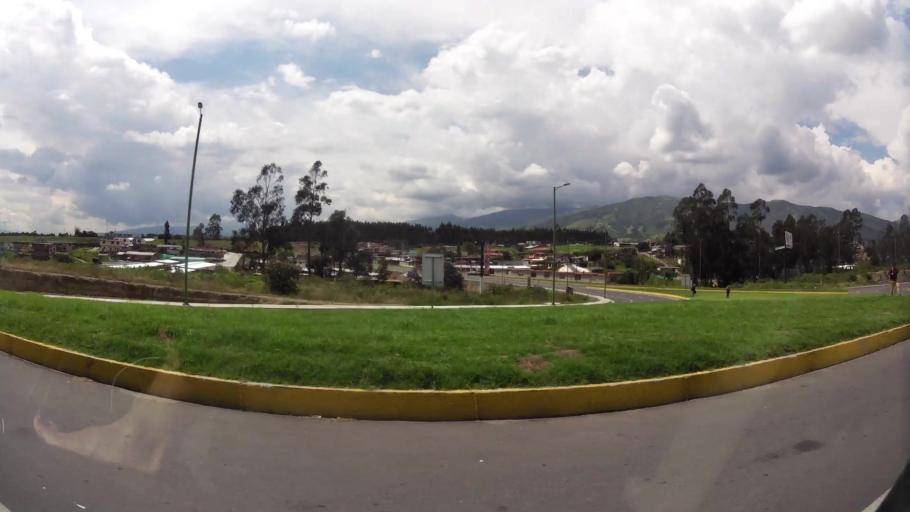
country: EC
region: Pichincha
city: Sangolqui
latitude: -0.1893
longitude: -78.3391
